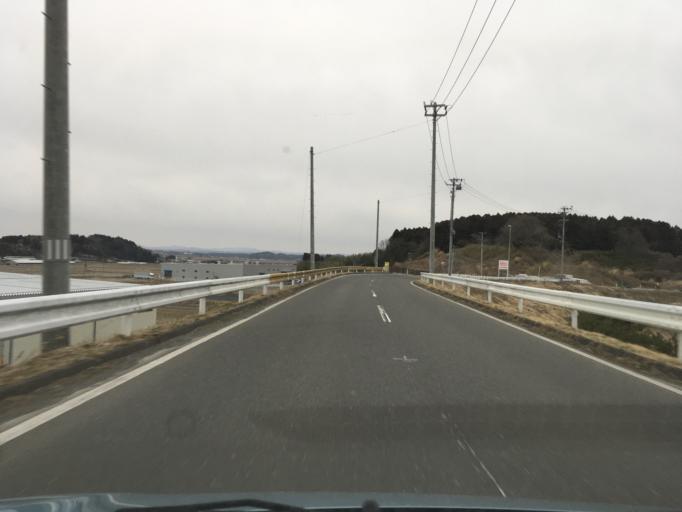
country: JP
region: Miyagi
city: Wakuya
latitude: 38.6988
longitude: 141.1688
